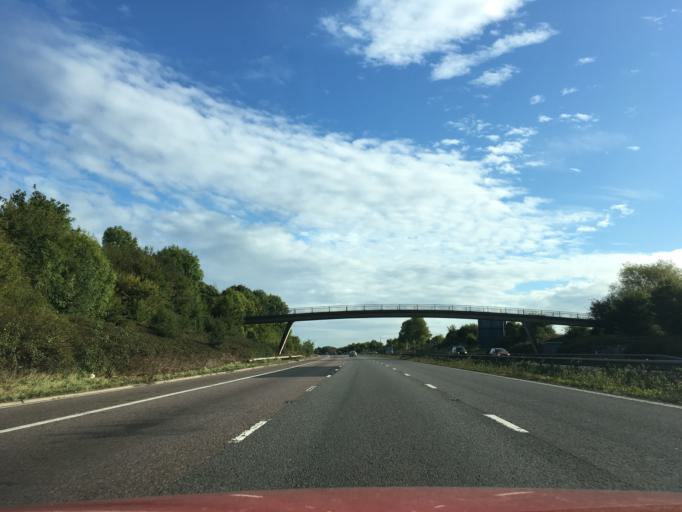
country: GB
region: England
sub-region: Gloucestershire
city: Churchdown
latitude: 51.8627
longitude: -2.1661
